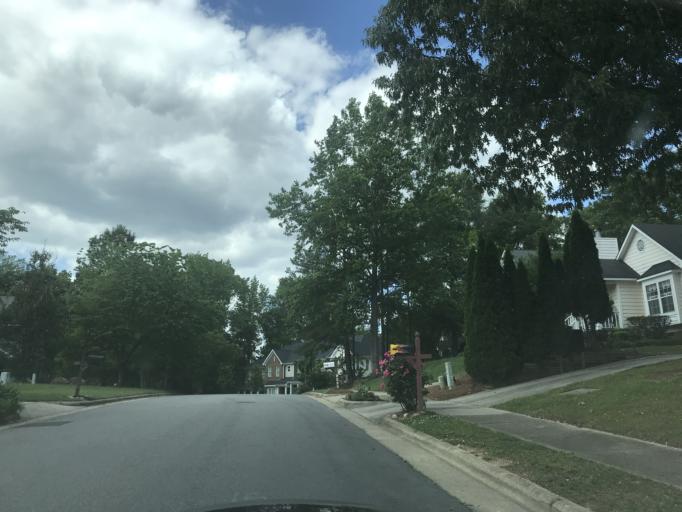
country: US
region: North Carolina
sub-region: Wake County
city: Raleigh
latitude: 35.8120
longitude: -78.6214
